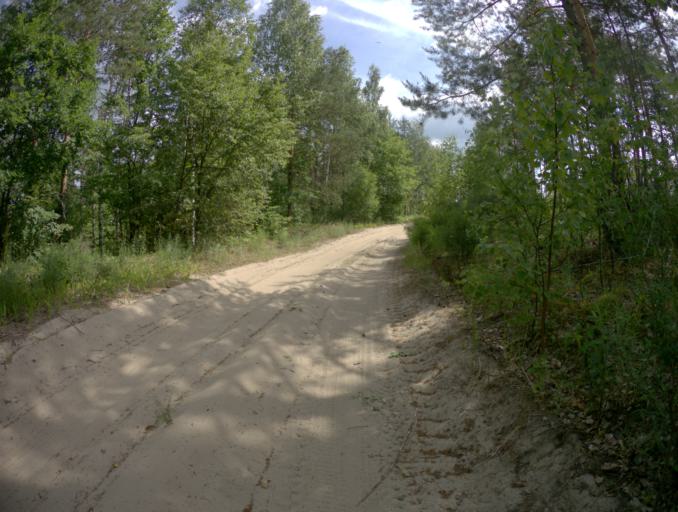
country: RU
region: Ivanovo
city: Talitsy
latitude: 56.5362
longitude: 42.4449
